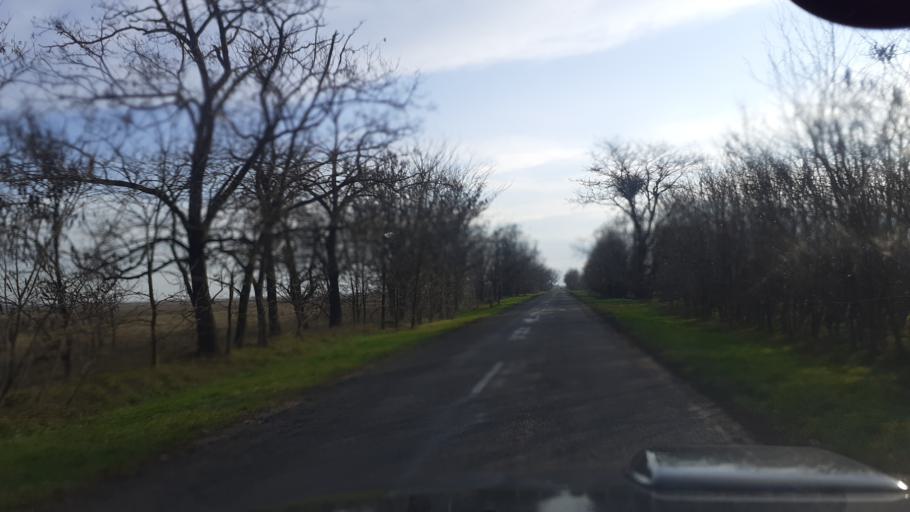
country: HU
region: Bacs-Kiskun
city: Kunszentmiklos
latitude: 47.0945
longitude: 19.0931
